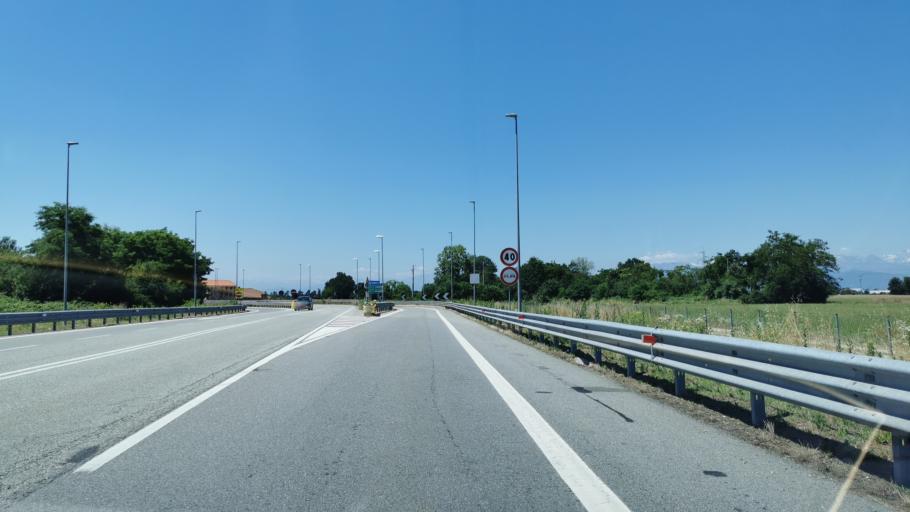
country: IT
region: Piedmont
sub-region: Provincia di Torino
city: Brandizzo
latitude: 45.1834
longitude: 7.8269
